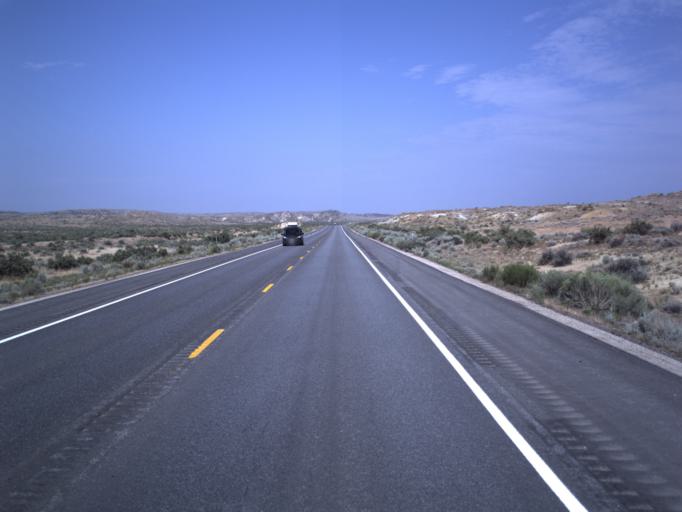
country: US
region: Colorado
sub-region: Rio Blanco County
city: Rangely
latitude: 40.2853
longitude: -109.1232
